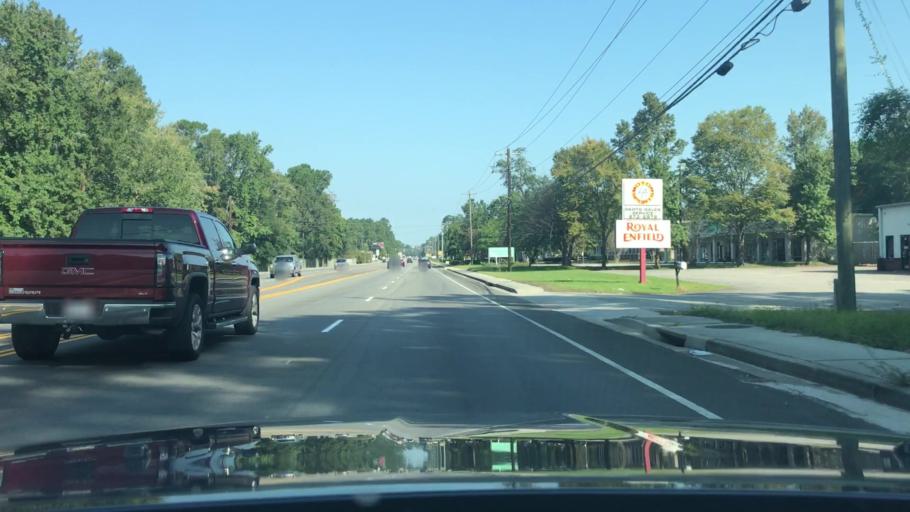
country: US
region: South Carolina
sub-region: Dorchester County
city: Centerville
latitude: 32.9783
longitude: -80.1732
